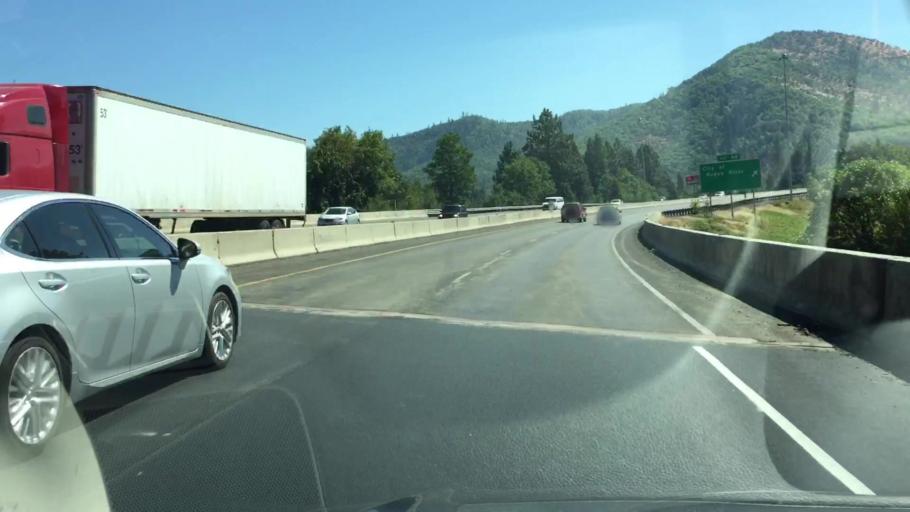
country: US
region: Oregon
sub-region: Jackson County
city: Rogue River
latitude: 42.4341
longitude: -123.1749
